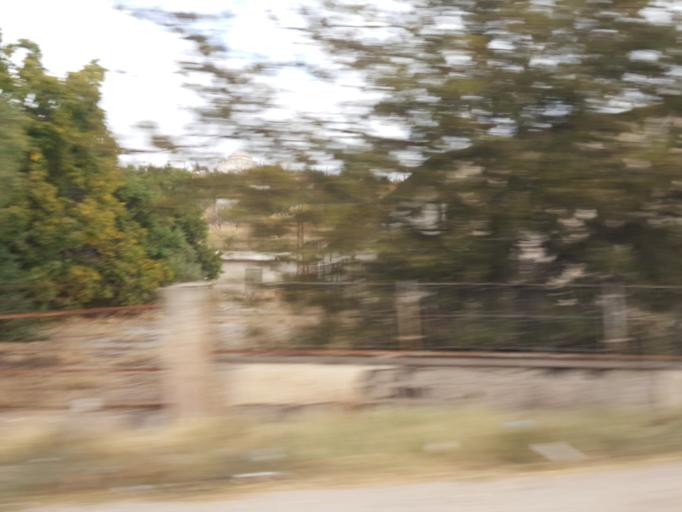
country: TR
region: Kirikkale
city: Keskin
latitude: 39.6743
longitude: 33.6034
